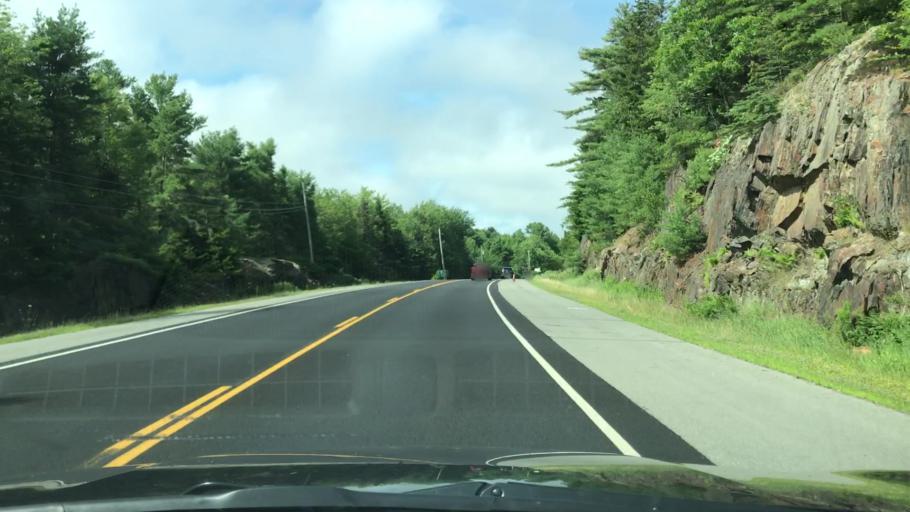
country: US
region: Maine
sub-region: Hancock County
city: Bucksport
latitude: 44.5414
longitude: -68.8097
